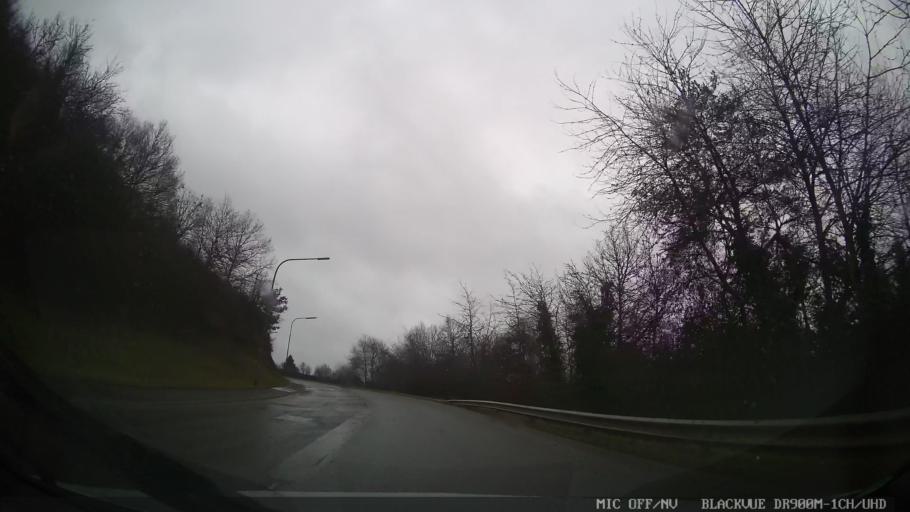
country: DE
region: Rheinland-Pfalz
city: Idar-Oberstein
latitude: 49.7151
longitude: 7.2896
